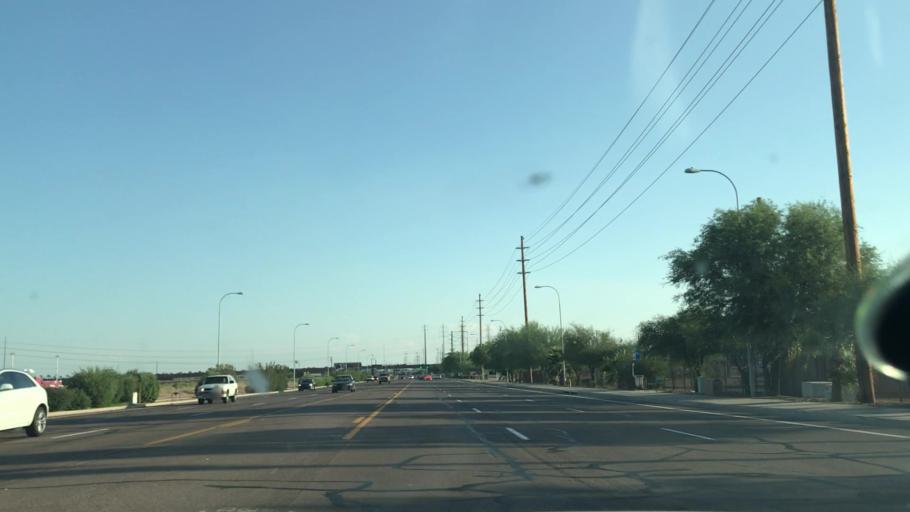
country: US
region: Arizona
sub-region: Maricopa County
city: Tempe
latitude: 33.4440
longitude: -111.9095
